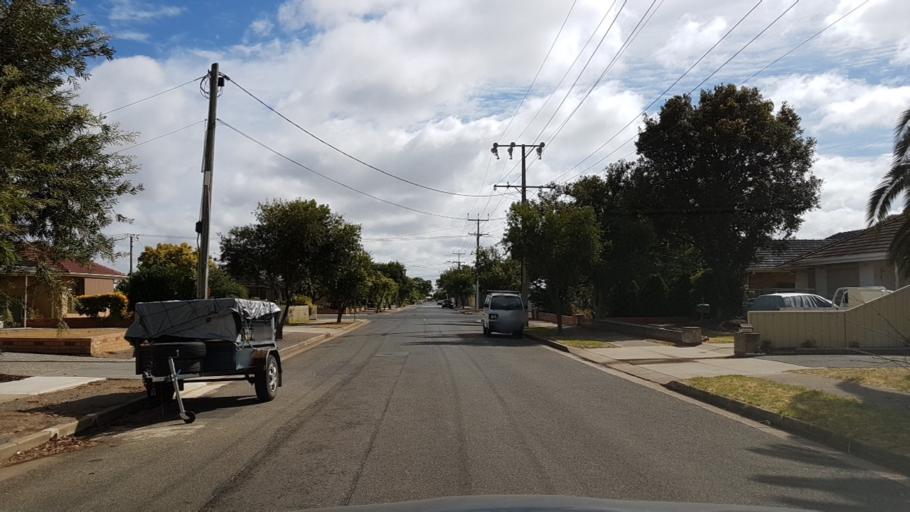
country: AU
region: South Australia
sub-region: Marion
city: Plympton Park
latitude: -34.9889
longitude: 138.5503
